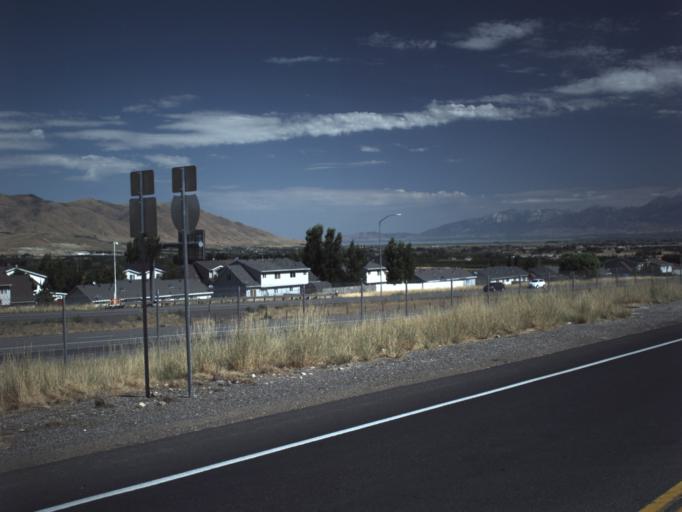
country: US
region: Utah
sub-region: Utah County
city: Santaquin
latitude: 39.9782
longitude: -111.7691
